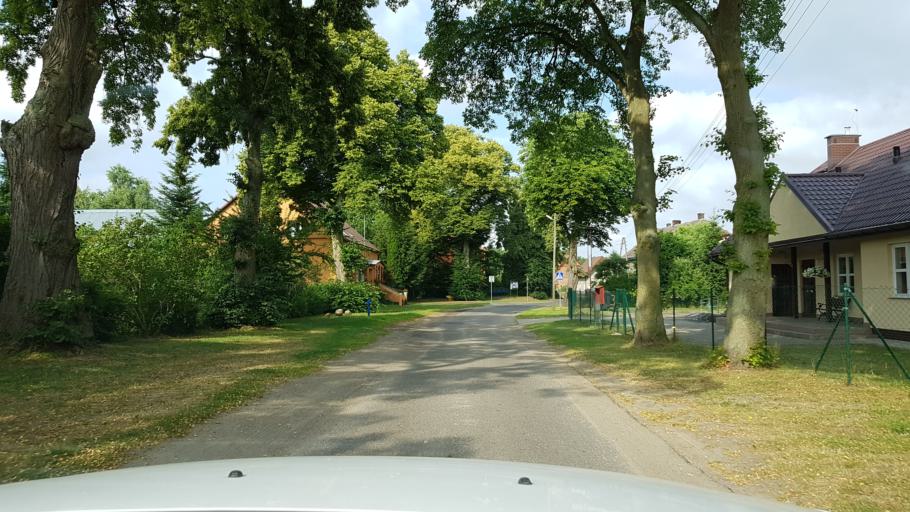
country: PL
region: West Pomeranian Voivodeship
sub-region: Powiat gryfinski
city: Gryfino
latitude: 53.2335
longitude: 14.5552
